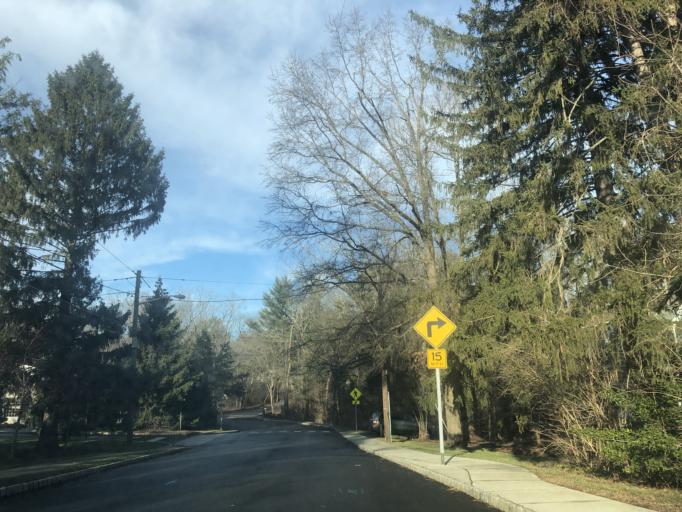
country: US
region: New Jersey
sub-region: Somerset County
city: Kingston
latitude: 40.3656
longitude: -74.6291
